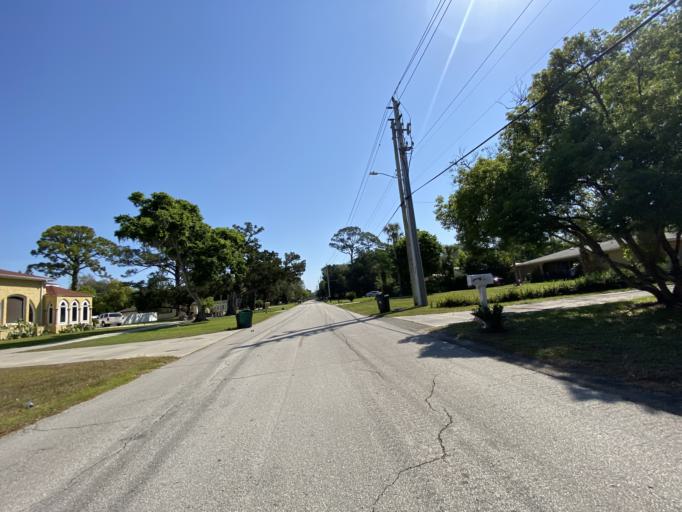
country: US
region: Florida
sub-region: Volusia County
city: South Daytona
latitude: 29.1644
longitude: -81.0077
